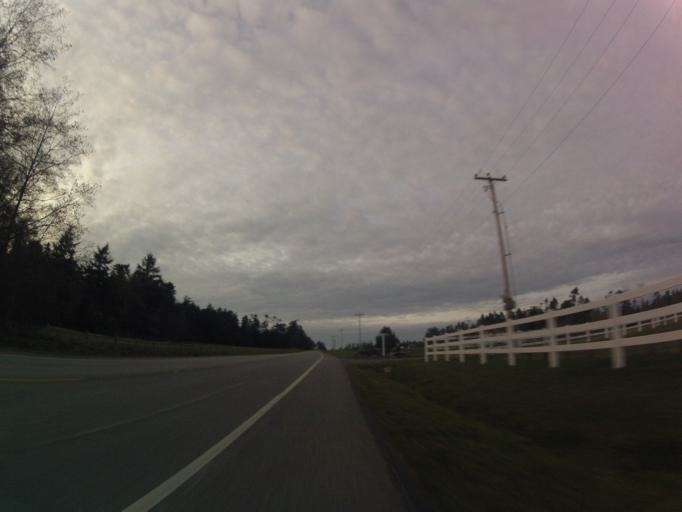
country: US
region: Washington
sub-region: Island County
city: Coupeville
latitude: 48.1726
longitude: -122.6805
